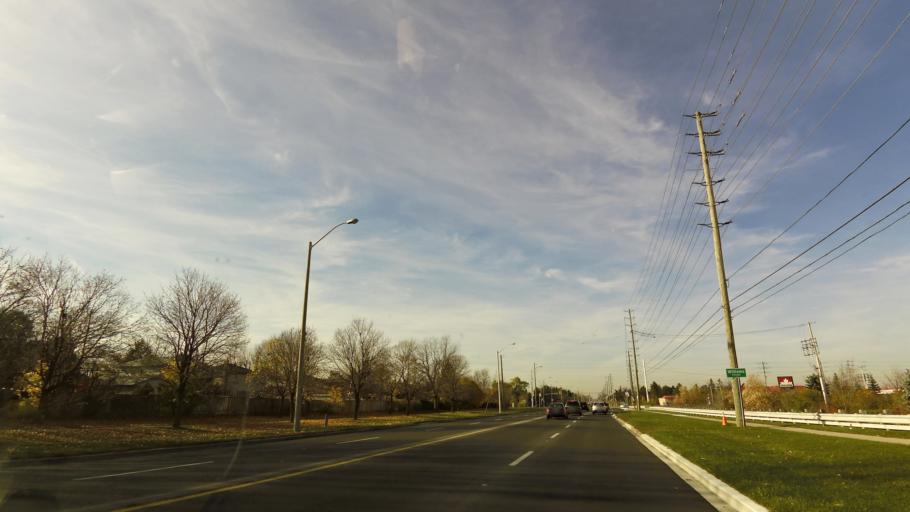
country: CA
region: Ontario
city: Brampton
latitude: 43.7428
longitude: -79.7183
